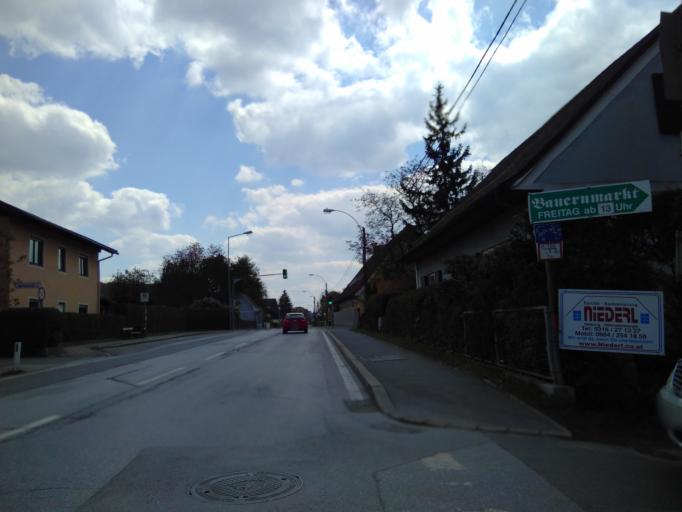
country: AT
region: Styria
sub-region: Politischer Bezirk Graz-Umgebung
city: Feldkirchen bei Graz
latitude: 47.0277
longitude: 15.4667
